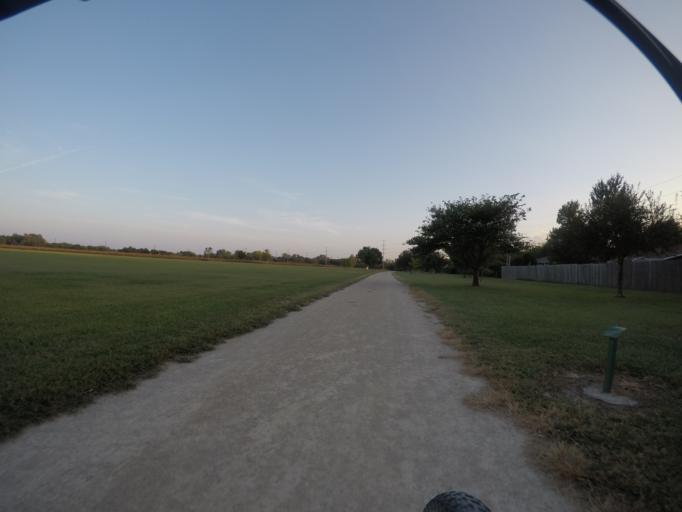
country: US
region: Kansas
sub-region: Riley County
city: Manhattan
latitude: 39.2009
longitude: -96.5499
